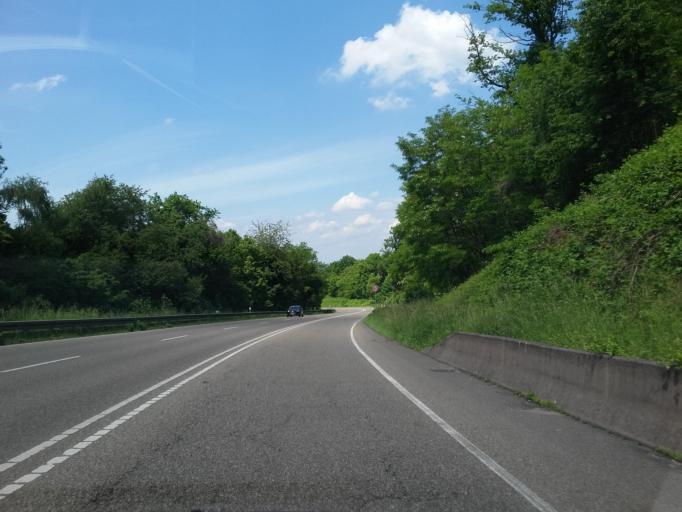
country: DE
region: Baden-Wuerttemberg
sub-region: Regierungsbezirk Stuttgart
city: Flein
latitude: 49.1106
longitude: 9.2337
